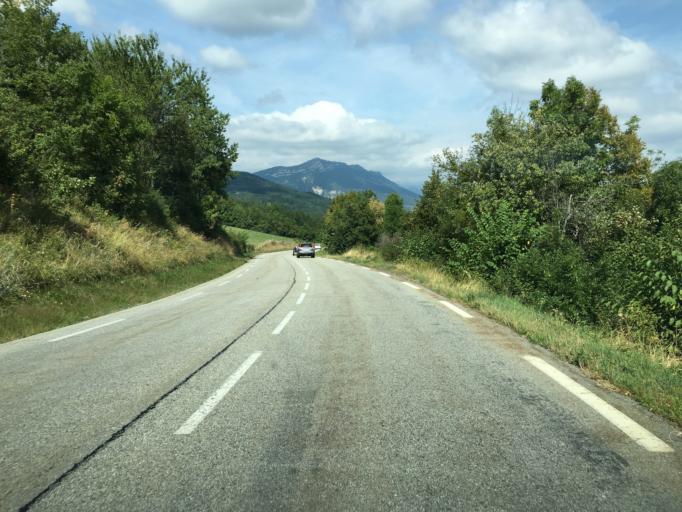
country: FR
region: Rhone-Alpes
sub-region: Departement de l'Isere
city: Mens
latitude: 44.7504
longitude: 5.6741
